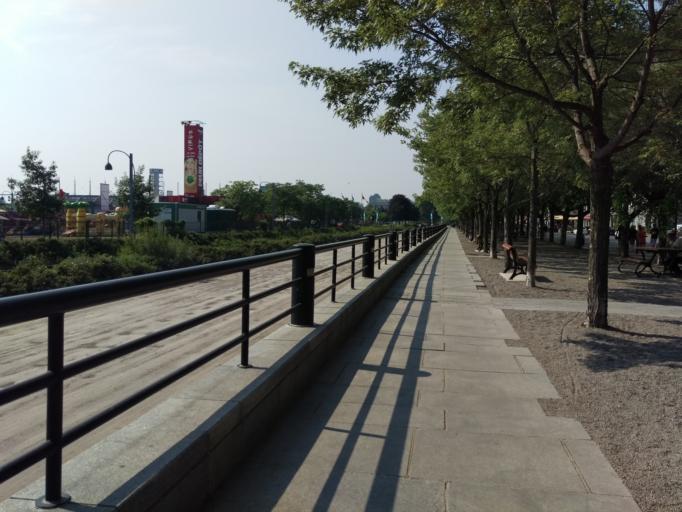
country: CA
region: Quebec
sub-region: Montreal
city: Montreal
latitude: 45.5088
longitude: -73.5510
